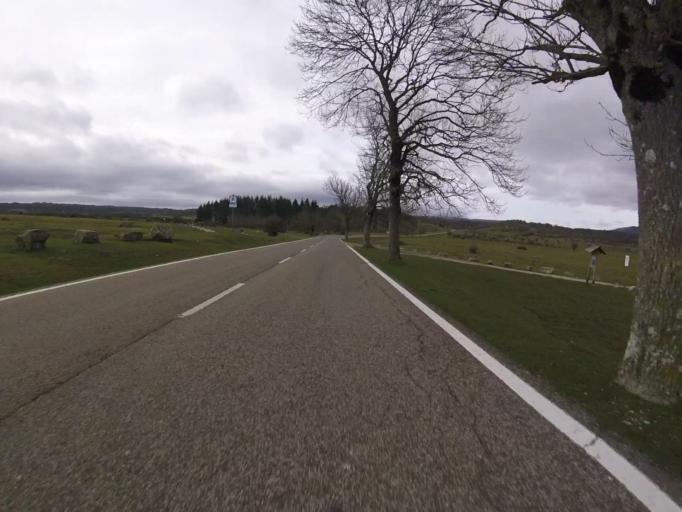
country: ES
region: Navarre
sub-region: Provincia de Navarra
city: Eulate
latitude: 42.8106
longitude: -2.1587
